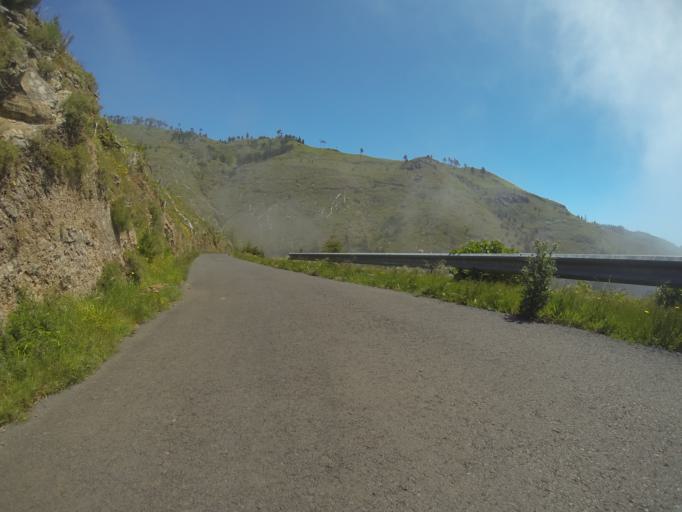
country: PT
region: Madeira
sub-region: Funchal
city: Nossa Senhora do Monte
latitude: 32.7016
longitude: -16.9097
